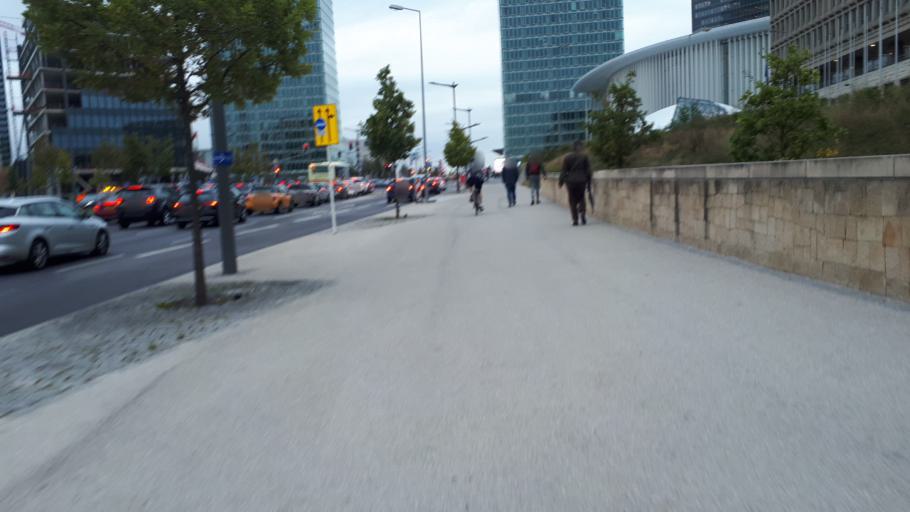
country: LU
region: Luxembourg
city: Kirchberg
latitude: 49.6187
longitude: 6.1399
